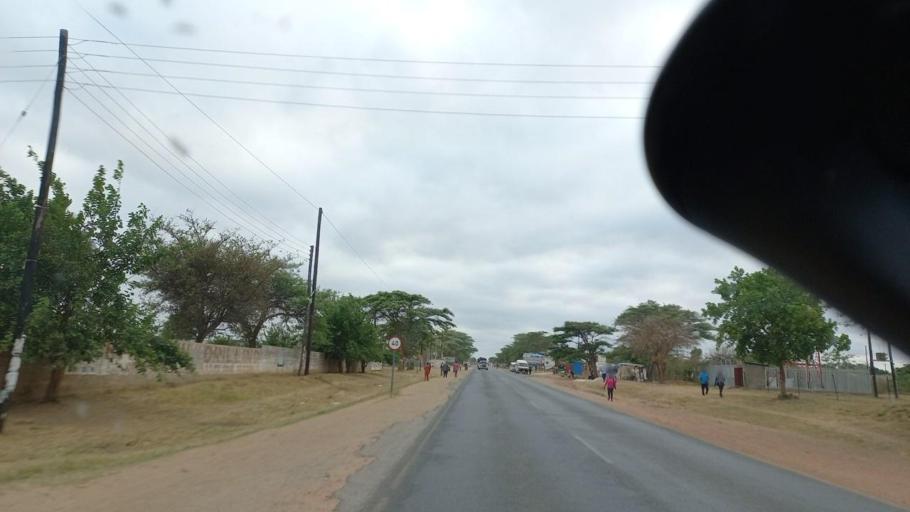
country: ZM
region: Lusaka
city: Chongwe
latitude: -15.3385
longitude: 28.6674
